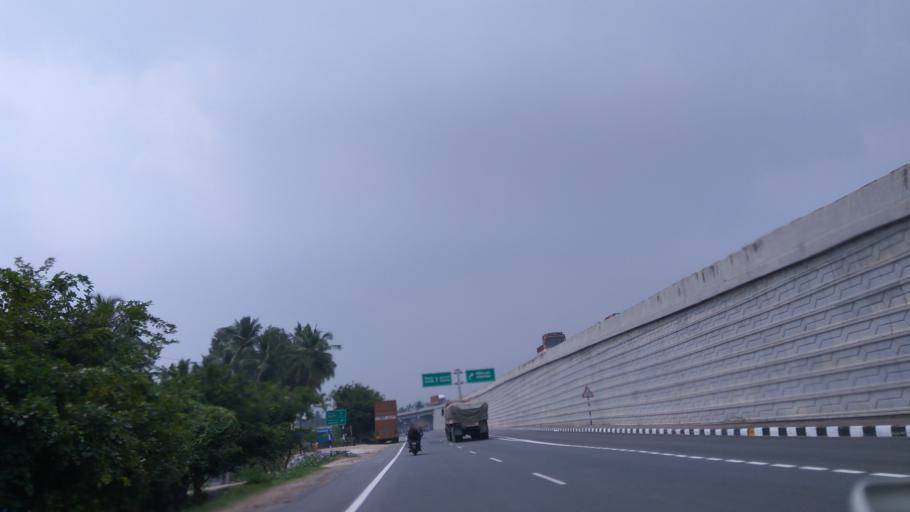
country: IN
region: Tamil Nadu
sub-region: Krishnagiri
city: Kaverippattanam
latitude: 12.4027
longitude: 78.2198
